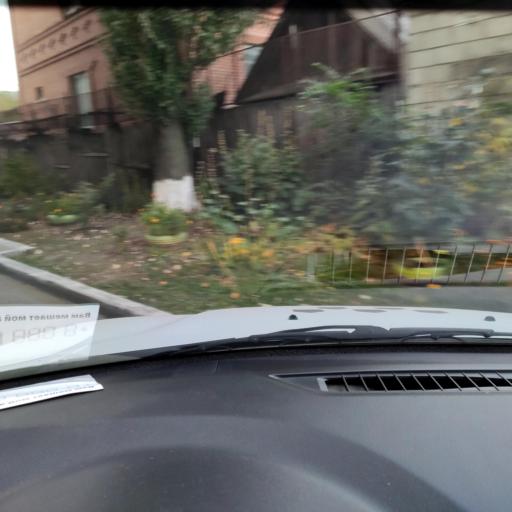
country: RU
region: Samara
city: Tol'yatti
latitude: 53.5239
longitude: 49.4139
